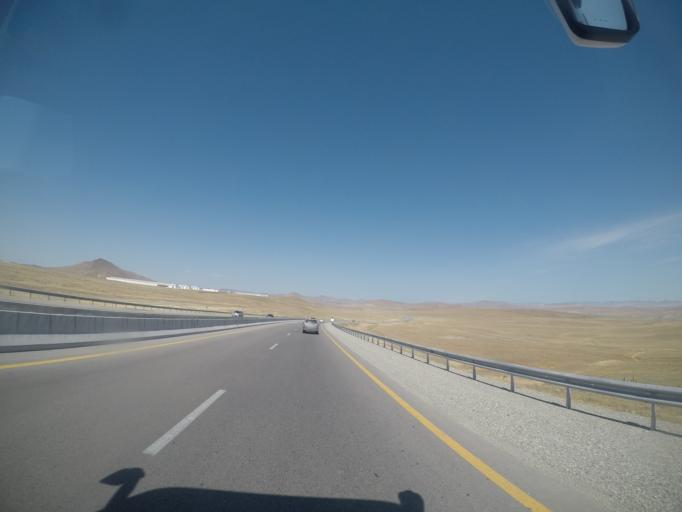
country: AZ
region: Sumqayit
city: Haci Zeynalabdin
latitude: 40.4849
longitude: 49.4106
